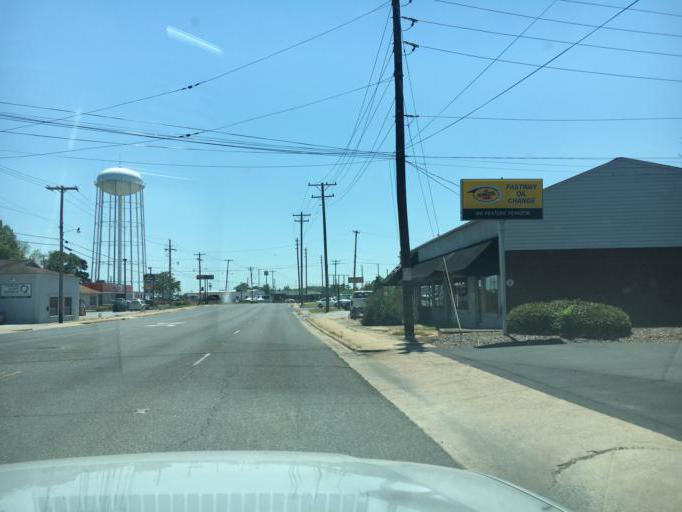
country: US
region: North Carolina
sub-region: Cleveland County
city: Shelby
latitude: 35.2829
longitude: -81.5409
